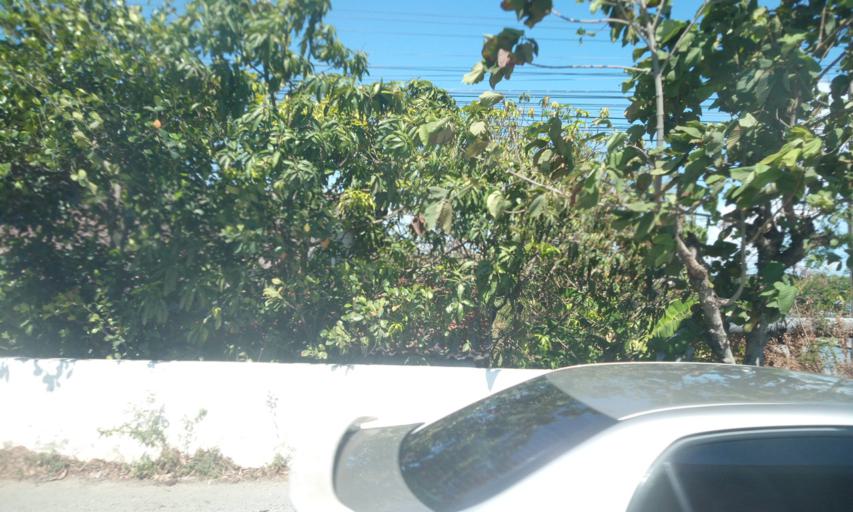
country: TH
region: Samut Prakan
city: Bang Bo District
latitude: 13.5137
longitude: 100.7885
